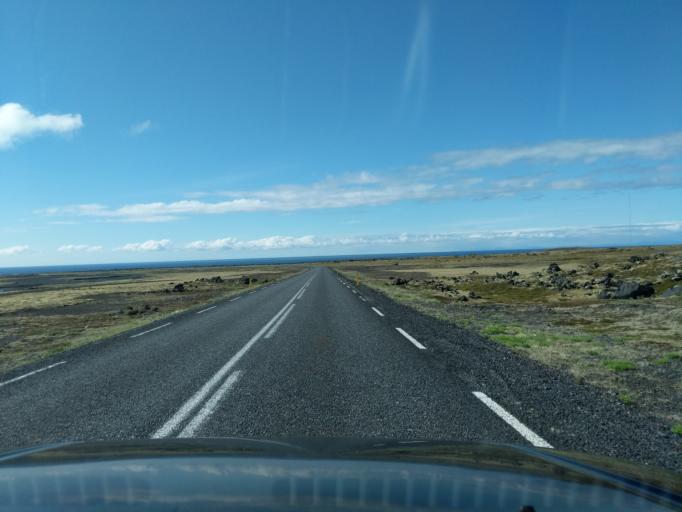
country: IS
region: West
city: Olafsvik
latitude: 64.8686
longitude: -23.9130
